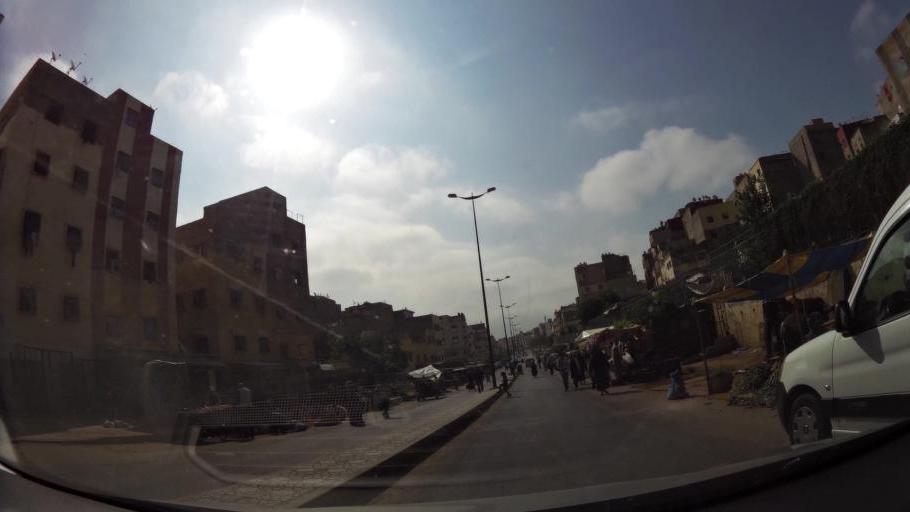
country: MA
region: Fes-Boulemane
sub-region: Fes
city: Fes
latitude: 34.0677
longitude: -5.0058
